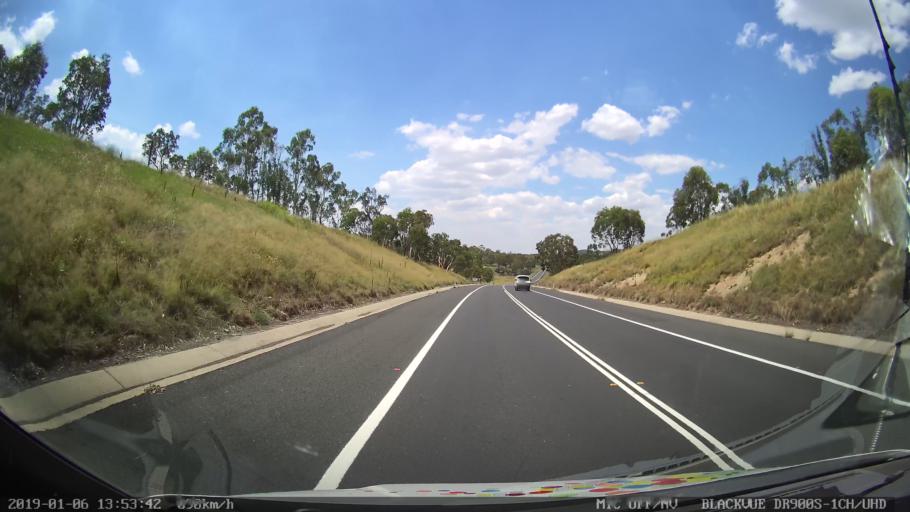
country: AU
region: New South Wales
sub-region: Tamworth Municipality
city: Kootingal
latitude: -30.9042
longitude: 151.1406
